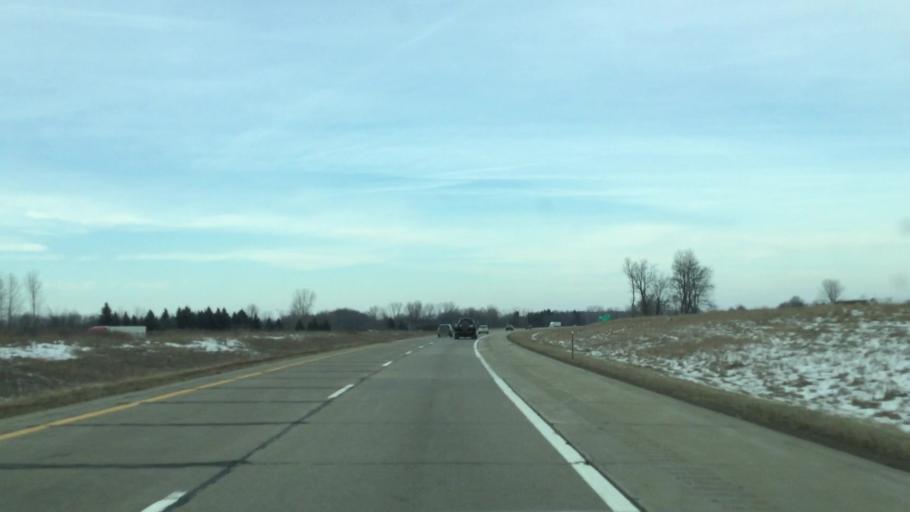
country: US
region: Michigan
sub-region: Eaton County
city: Charlotte
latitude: 42.4989
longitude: -84.8608
